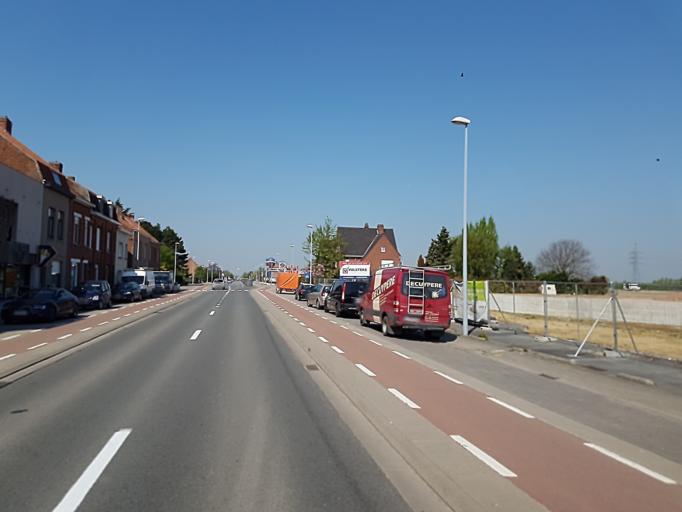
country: BE
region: Flanders
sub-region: Provincie West-Vlaanderen
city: Menen
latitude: 50.8014
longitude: 3.1048
